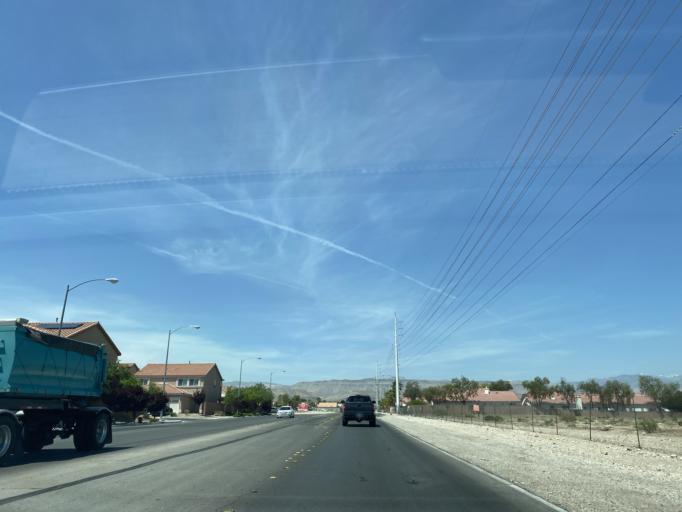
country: US
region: Nevada
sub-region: Clark County
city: Spring Valley
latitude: 36.0851
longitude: -115.2570
